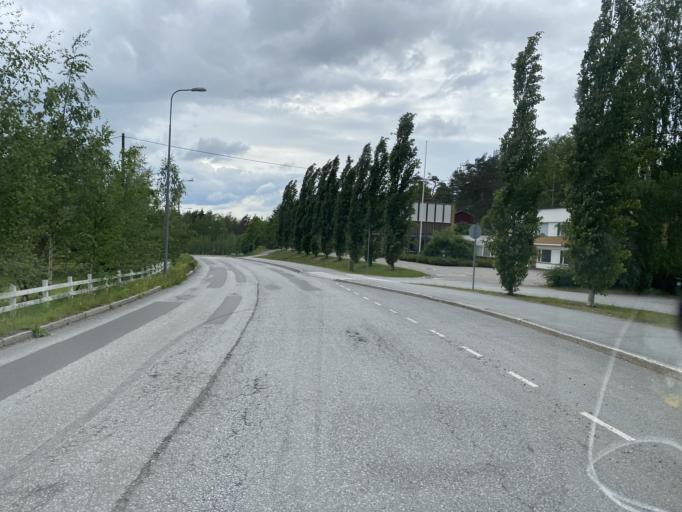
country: FI
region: Pirkanmaa
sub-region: Etelae-Pirkanmaa
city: Urjala
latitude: 61.0805
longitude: 23.5437
